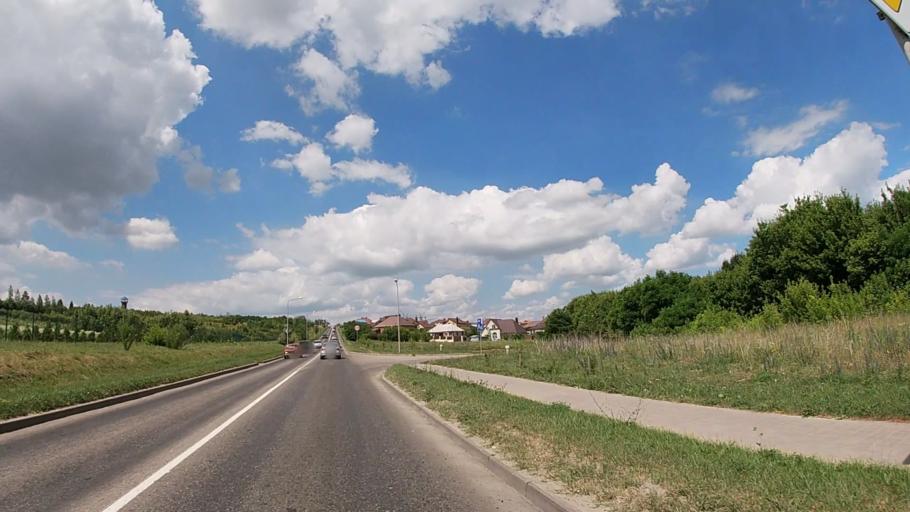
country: RU
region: Belgorod
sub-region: Belgorodskiy Rayon
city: Belgorod
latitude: 50.5951
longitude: 36.5488
